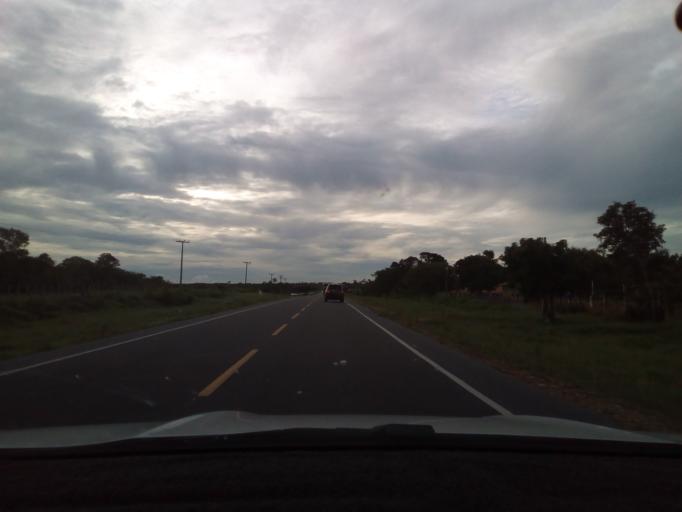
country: BR
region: Ceara
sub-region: Beberibe
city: Beberibe
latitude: -4.3630
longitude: -37.9547
